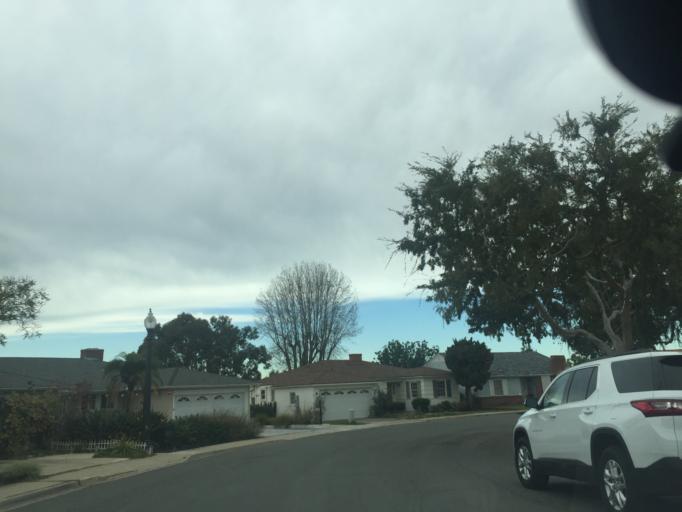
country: US
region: California
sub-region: San Diego County
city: Lemon Grove
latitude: 32.7661
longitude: -117.0912
